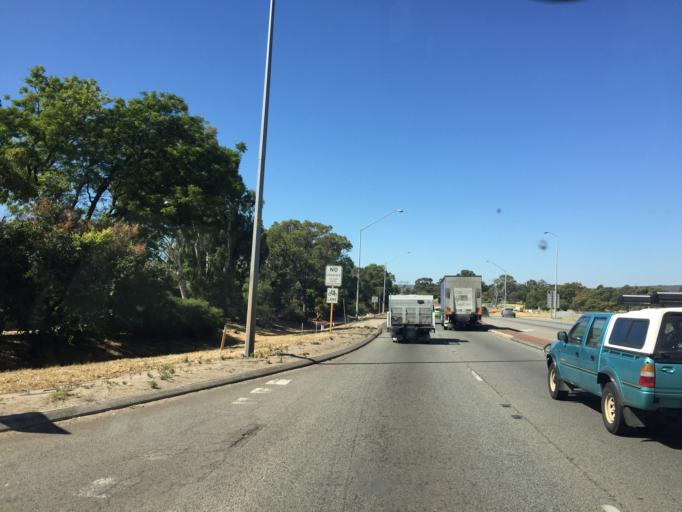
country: AU
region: Western Australia
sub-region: Kalamunda
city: Maida Vale
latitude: -31.9404
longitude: 116.0161
